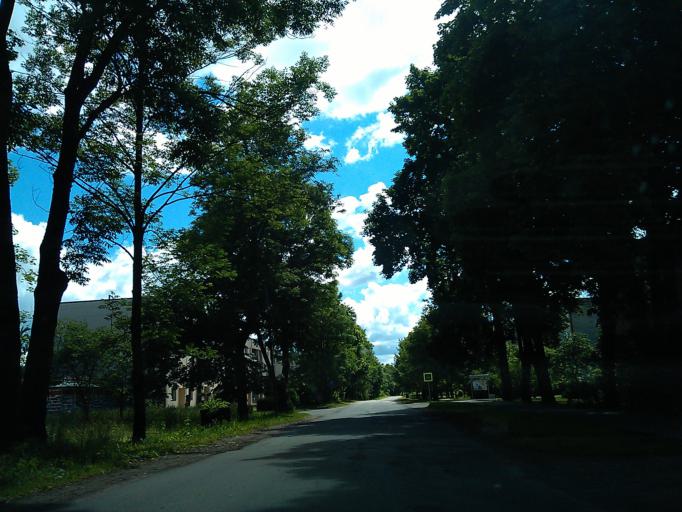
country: LV
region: Varaklani
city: Varaklani
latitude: 56.6097
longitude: 26.7595
